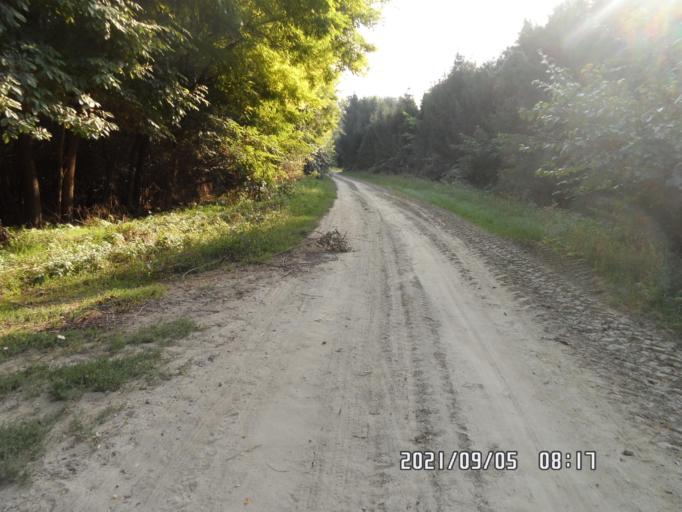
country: HU
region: Somogy
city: Marcali
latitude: 46.4990
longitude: 17.4177
